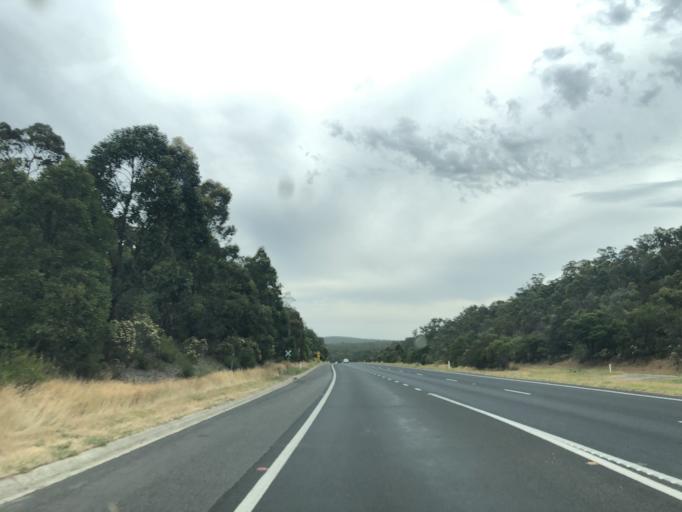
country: AU
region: Victoria
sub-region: Hume
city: Sunbury
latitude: -37.4182
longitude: 144.5440
